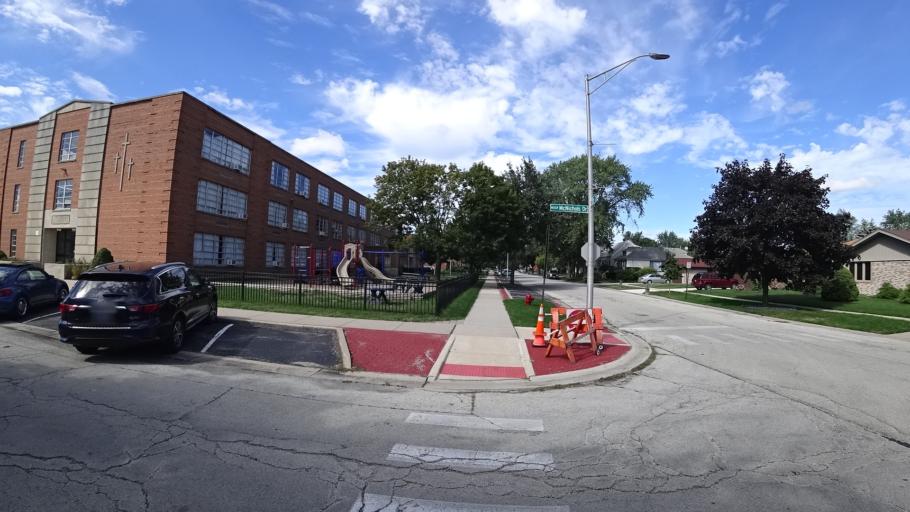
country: US
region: Illinois
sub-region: Cook County
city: Oak Lawn
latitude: 41.7216
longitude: -87.7593
